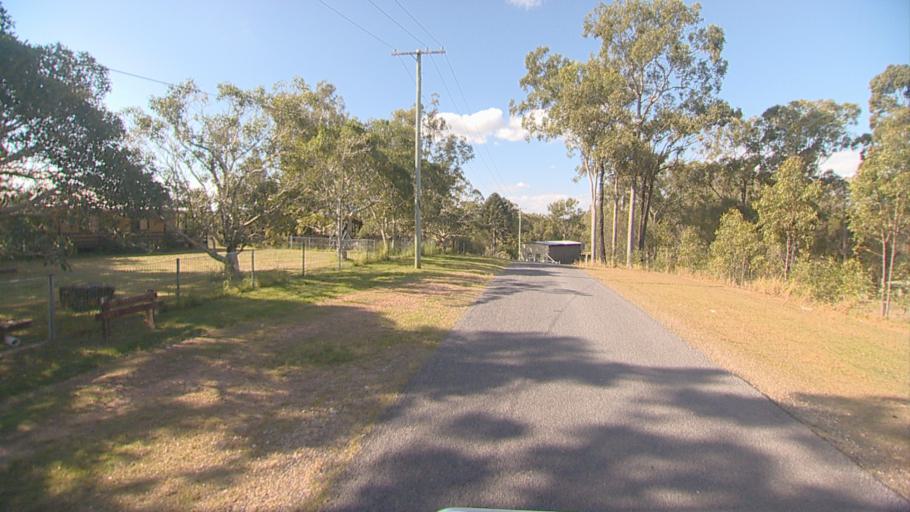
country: AU
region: Queensland
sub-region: Logan
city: Windaroo
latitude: -27.7394
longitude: 153.1579
